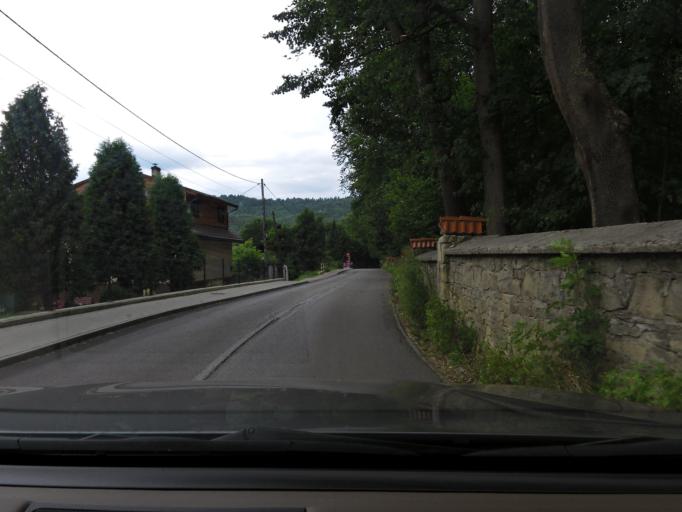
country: PL
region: Silesian Voivodeship
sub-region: Powiat zywiecki
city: Rajcza
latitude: 49.4986
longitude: 19.1014
